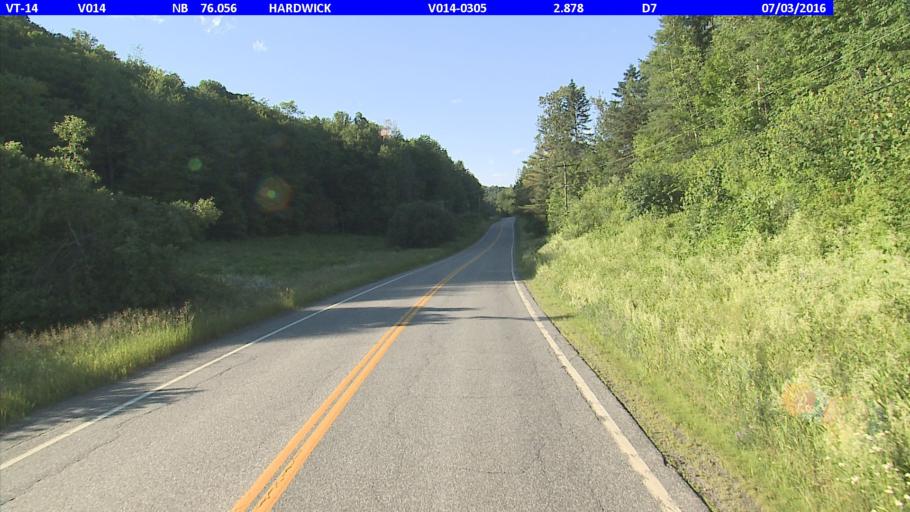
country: US
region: Vermont
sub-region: Caledonia County
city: Hardwick
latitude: 44.5357
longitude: -72.3743
